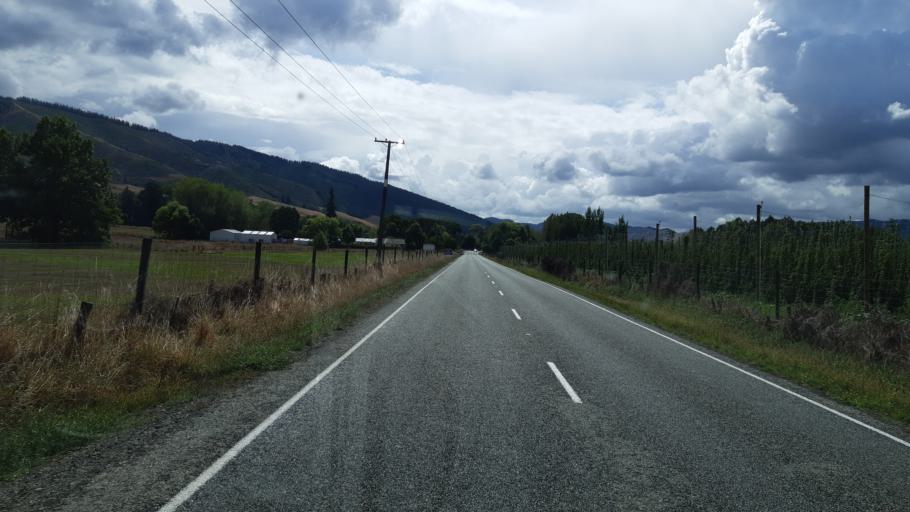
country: NZ
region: Tasman
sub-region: Tasman District
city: Wakefield
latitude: -41.4633
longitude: 172.8097
